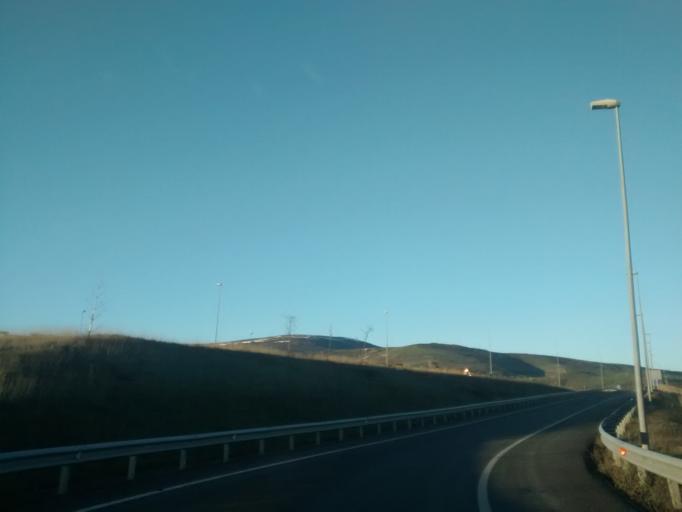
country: ES
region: Cantabria
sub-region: Provincia de Cantabria
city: Reinosa
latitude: 43.0073
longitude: -4.1242
